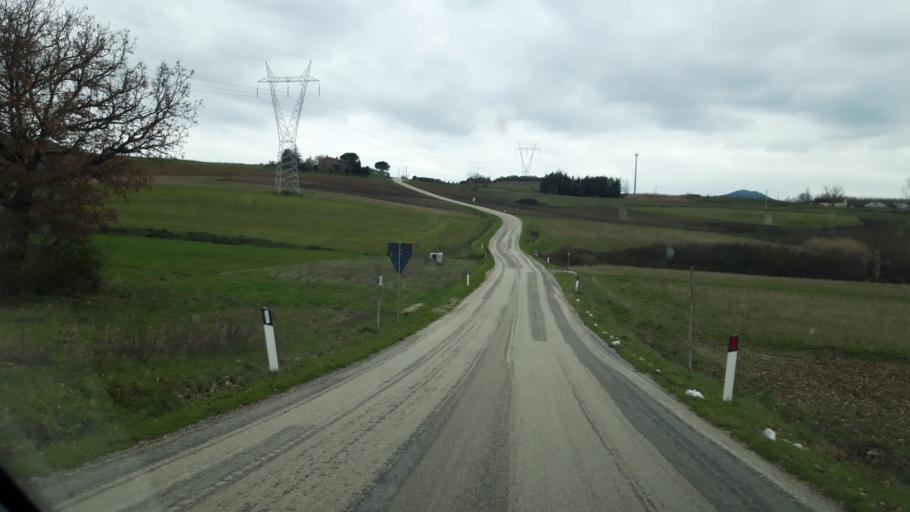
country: IT
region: Umbria
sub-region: Provincia di Perugia
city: Tavernelle
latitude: 42.9879
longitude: 12.1789
